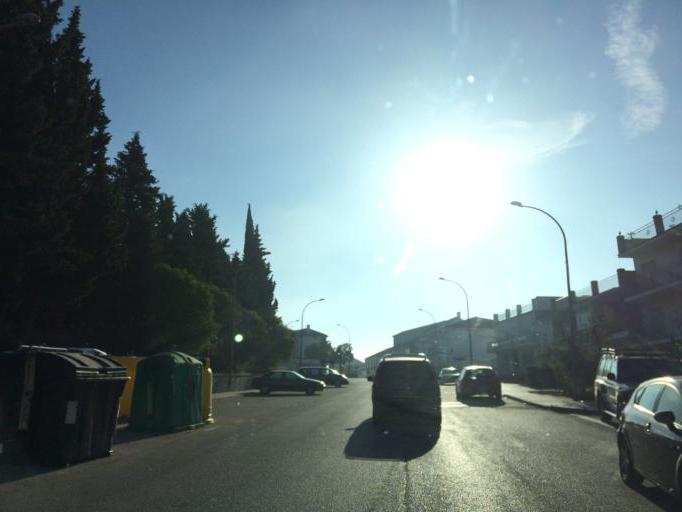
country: ES
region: Andalusia
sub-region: Provincia de Malaga
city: Colmenar
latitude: 36.9028
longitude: -4.3411
